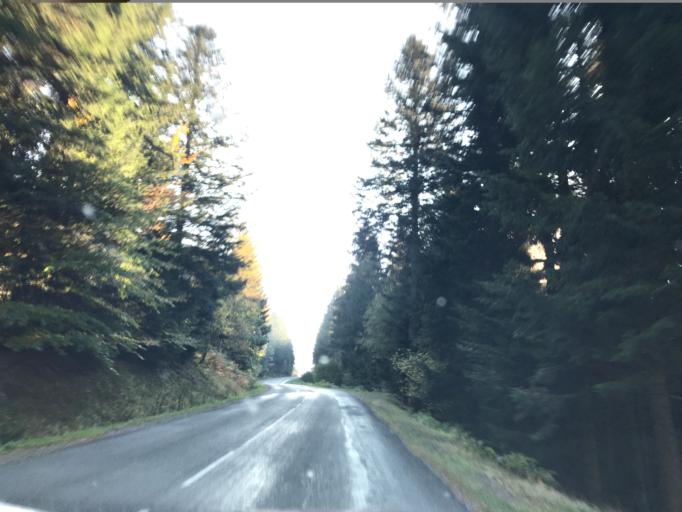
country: FR
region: Rhone-Alpes
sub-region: Departement de la Loire
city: Noiretable
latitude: 45.8056
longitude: 3.7182
